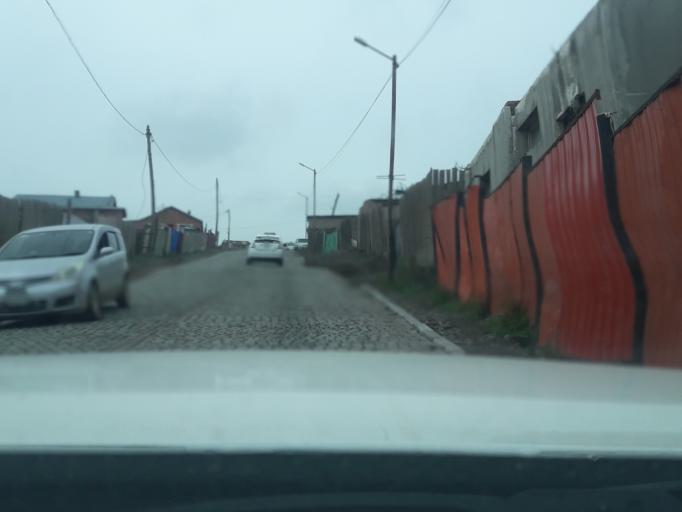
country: MN
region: Ulaanbaatar
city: Ulaanbaatar
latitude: 47.9509
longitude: 106.9070
